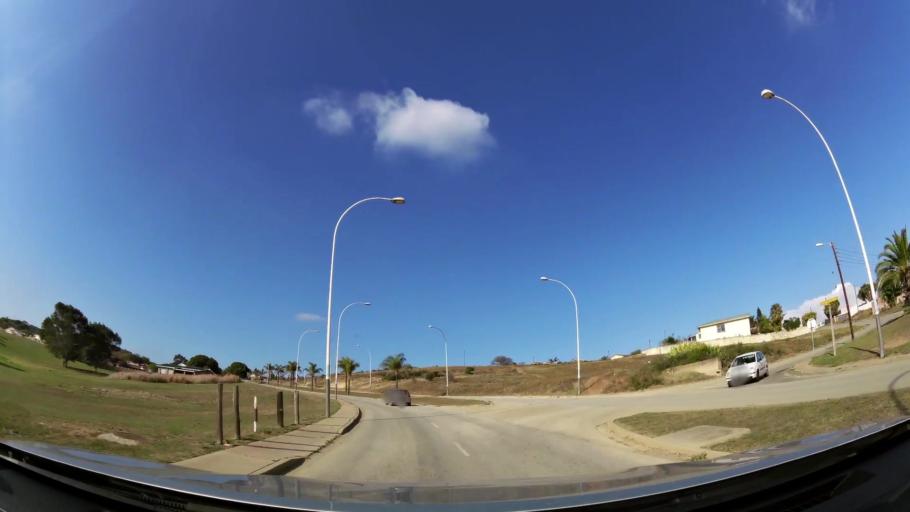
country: ZA
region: Eastern Cape
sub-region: Nelson Mandela Bay Metropolitan Municipality
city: Uitenhage
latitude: -33.7707
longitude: 25.4169
